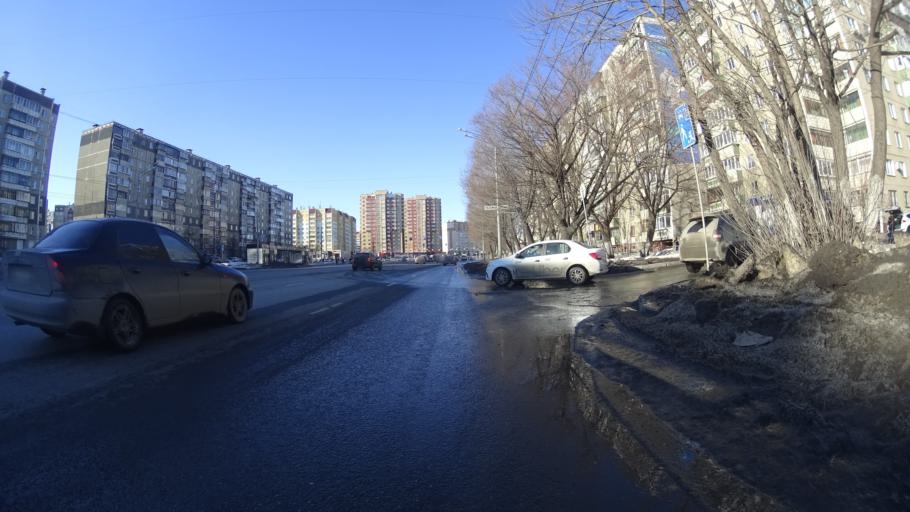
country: RU
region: Chelyabinsk
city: Roshchino
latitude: 55.1897
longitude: 61.2829
